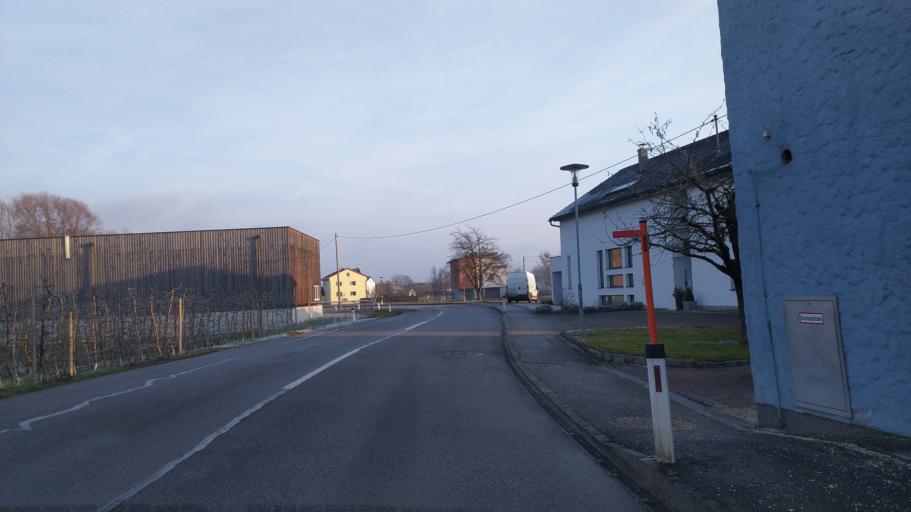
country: AT
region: Upper Austria
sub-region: Politischer Bezirk Urfahr-Umgebung
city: Goldworth
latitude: 48.3309
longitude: 14.1032
